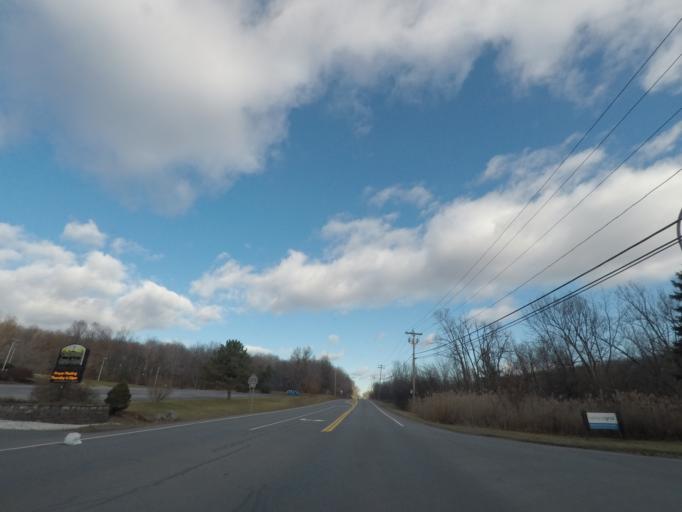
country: US
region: New York
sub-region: Saratoga County
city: Waterford
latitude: 42.7654
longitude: -73.6616
